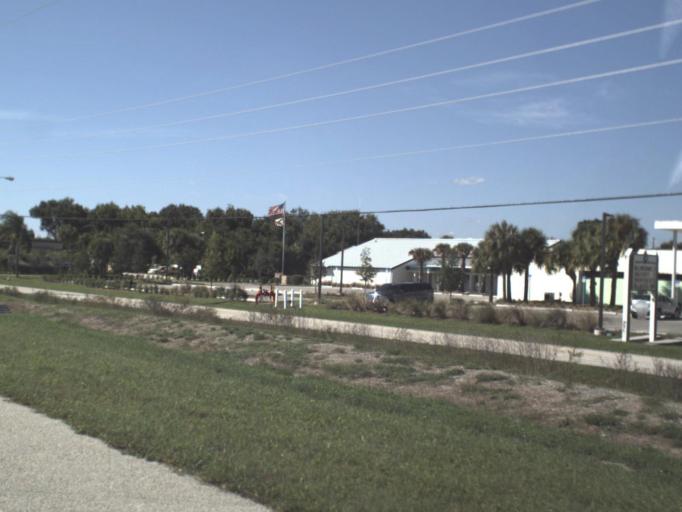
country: US
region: Florida
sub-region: Charlotte County
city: Grove City
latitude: 26.9344
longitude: -82.2927
